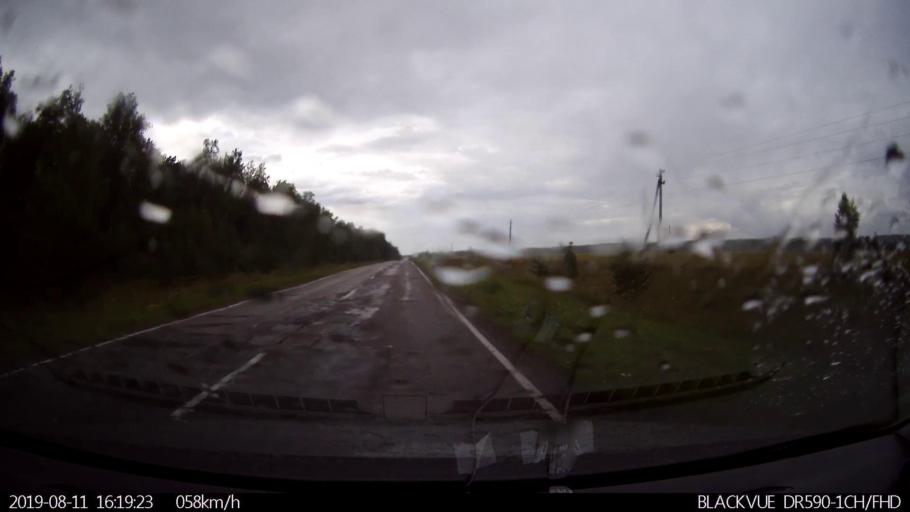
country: RU
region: Ulyanovsk
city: Mayna
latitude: 54.0633
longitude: 47.6077
